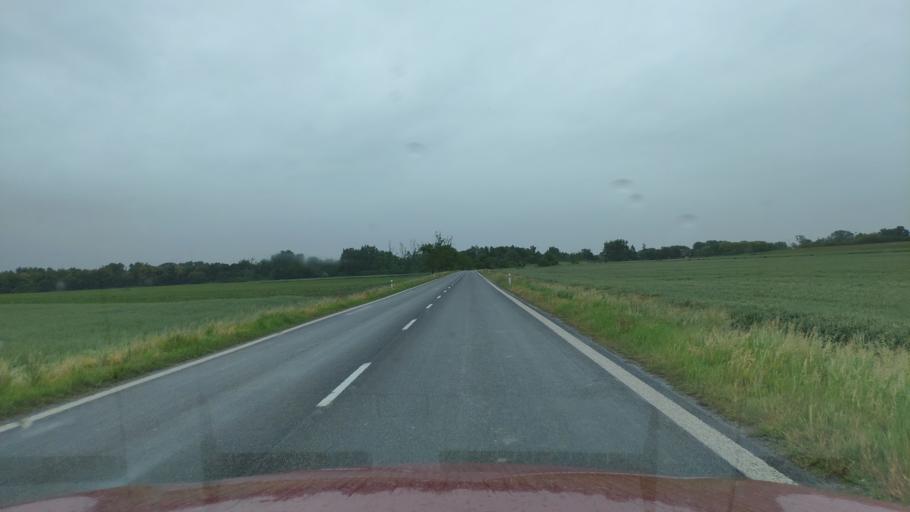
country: HU
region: Borsod-Abauj-Zemplen
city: Karcsa
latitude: 48.4298
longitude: 21.8488
